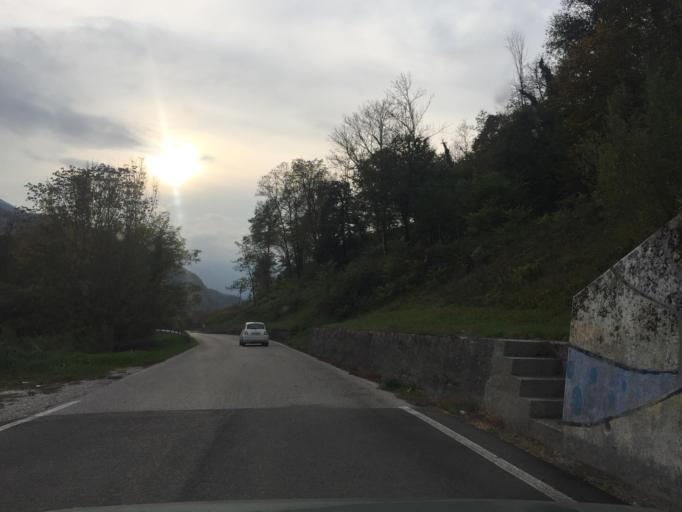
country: IT
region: Friuli Venezia Giulia
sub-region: Provincia di Pordenone
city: Andreis
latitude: 46.2001
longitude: 12.6157
